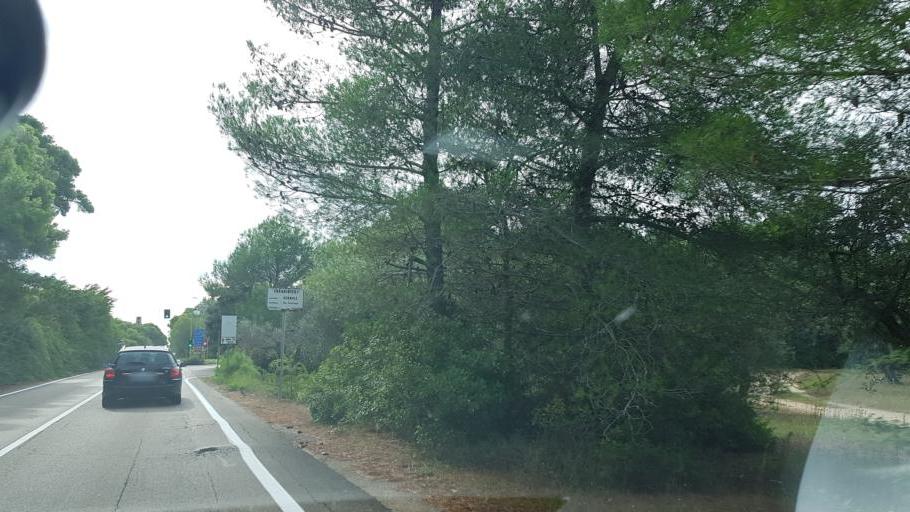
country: IT
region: Apulia
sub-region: Provincia di Lecce
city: Struda
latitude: 40.3690
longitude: 18.3094
